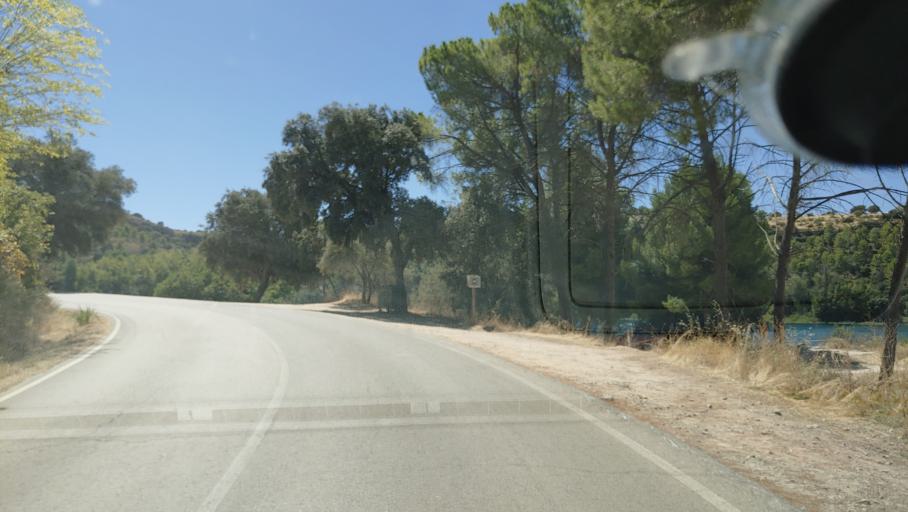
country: ES
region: Castille-La Mancha
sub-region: Provincia de Ciudad Real
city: Ruidera
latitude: 38.9524
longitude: -2.8631
